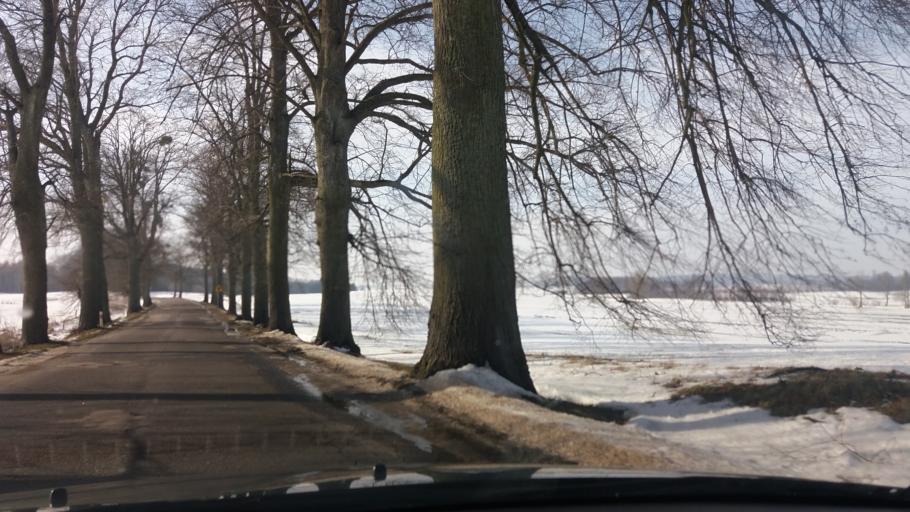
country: PL
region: Warmian-Masurian Voivodeship
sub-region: Powiat bartoszycki
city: Bisztynek
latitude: 54.1090
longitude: 20.8323
